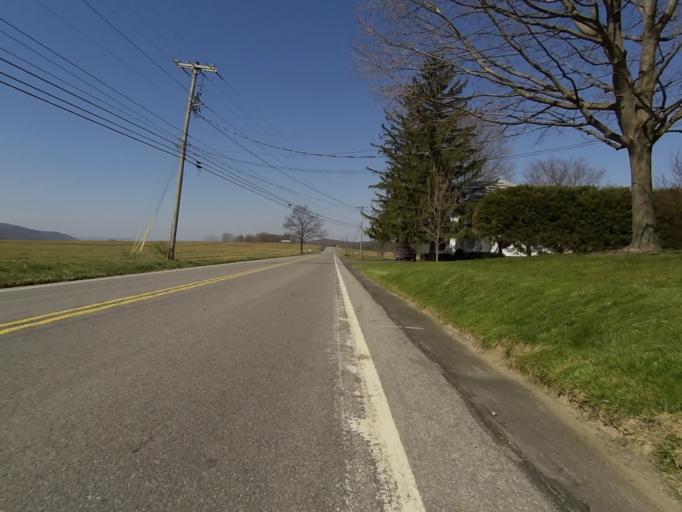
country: US
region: Pennsylvania
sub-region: Centre County
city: Stormstown
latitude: 40.7022
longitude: -77.9960
